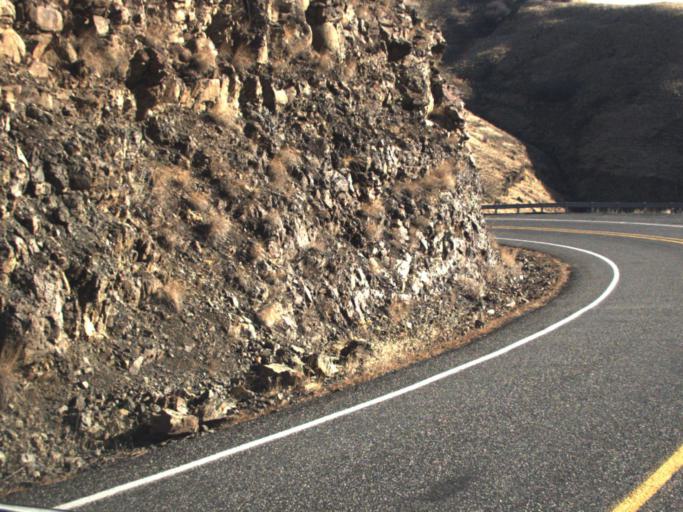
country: US
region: Washington
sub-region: Asotin County
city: Asotin
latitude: 46.0529
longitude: -117.2340
